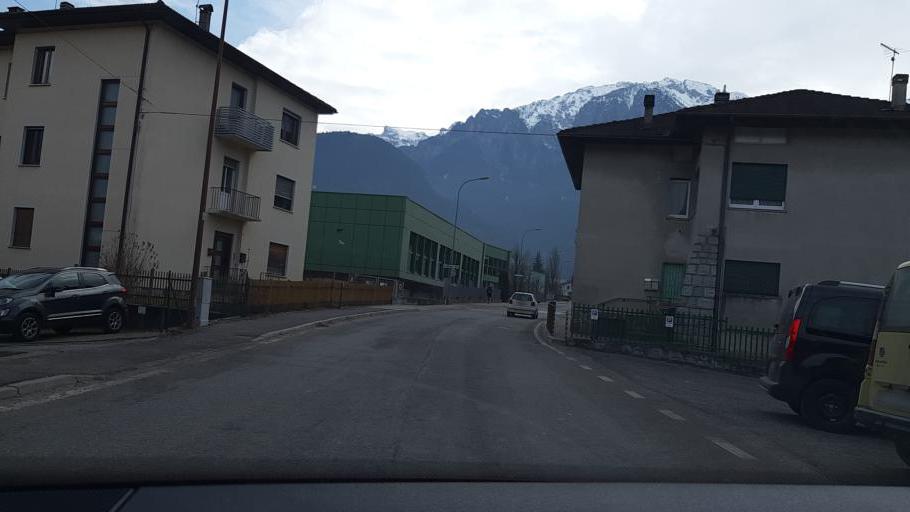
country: IT
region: Trentino-Alto Adige
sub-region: Provincia di Trento
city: Borgo
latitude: 46.0500
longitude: 11.4570
